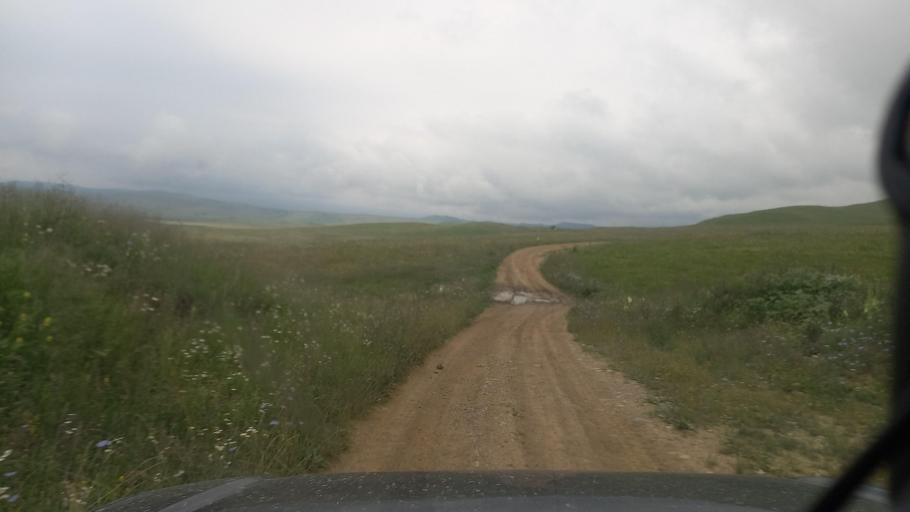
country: RU
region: Karachayevo-Cherkesiya
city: Pregradnaya
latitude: 43.9977
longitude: 41.1874
